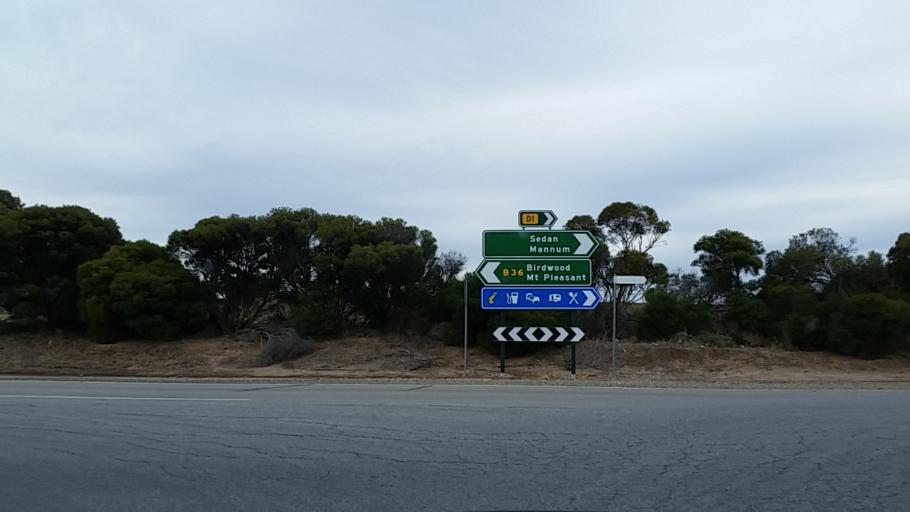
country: AU
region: South Australia
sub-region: Mid Murray
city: Mannum
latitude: -34.9039
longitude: 139.2817
